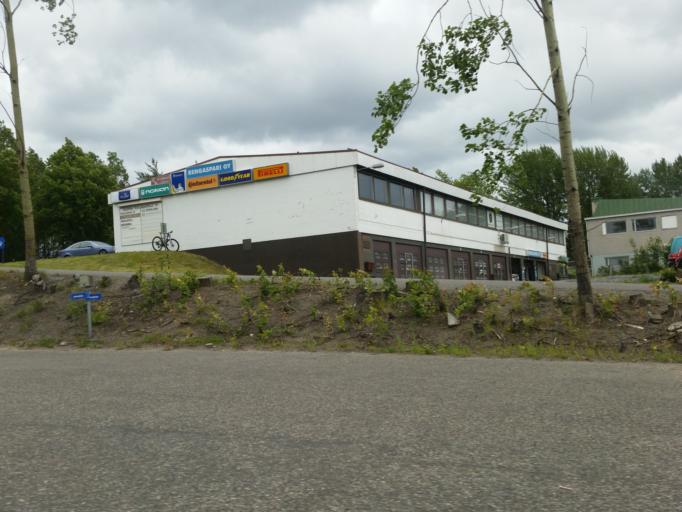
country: FI
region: Northern Savo
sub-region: Kuopio
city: Kuopio
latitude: 62.8975
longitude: 27.7080
